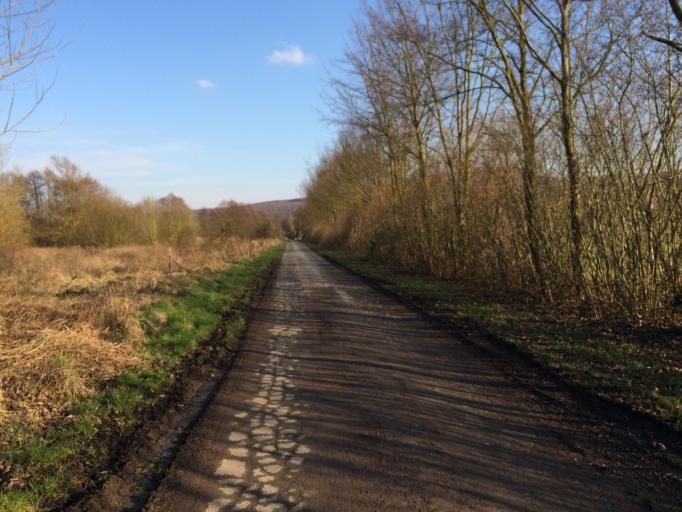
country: DE
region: North Rhine-Westphalia
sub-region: Regierungsbezirk Detmold
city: Blomberg
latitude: 51.9216
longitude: 9.1431
